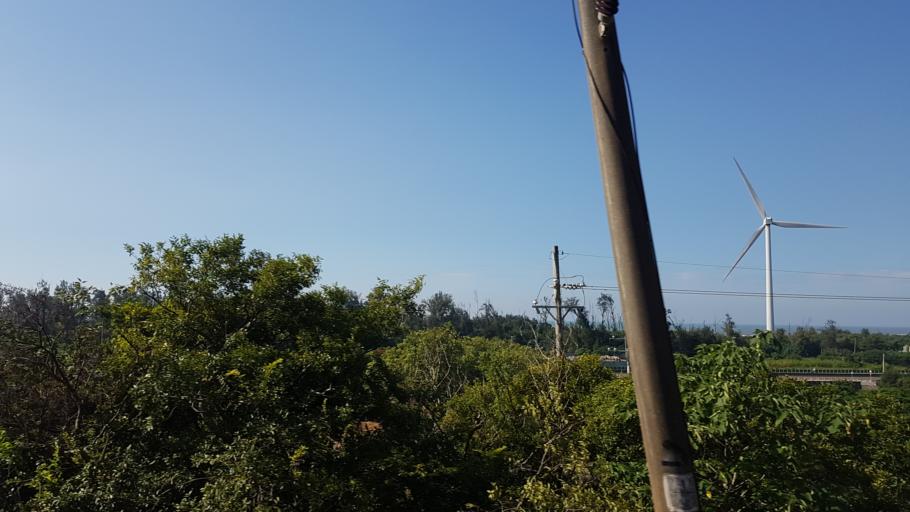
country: TW
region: Taiwan
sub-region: Hsinchu
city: Hsinchu
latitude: 24.7335
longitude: 120.8843
